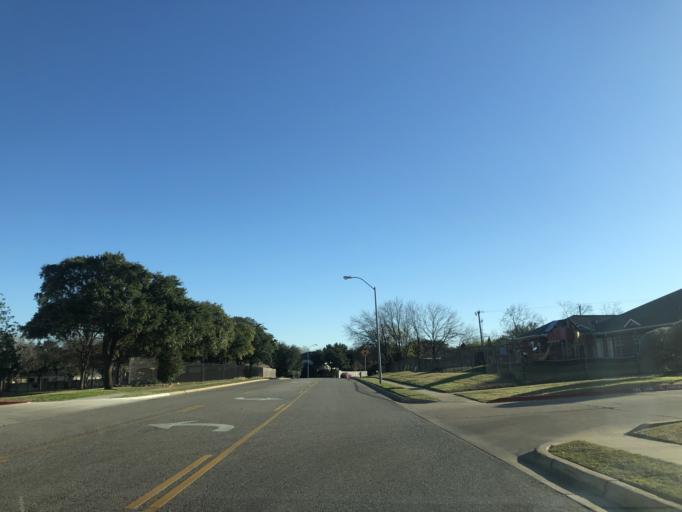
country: US
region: Texas
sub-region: Travis County
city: Windemere
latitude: 30.4830
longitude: -97.6548
